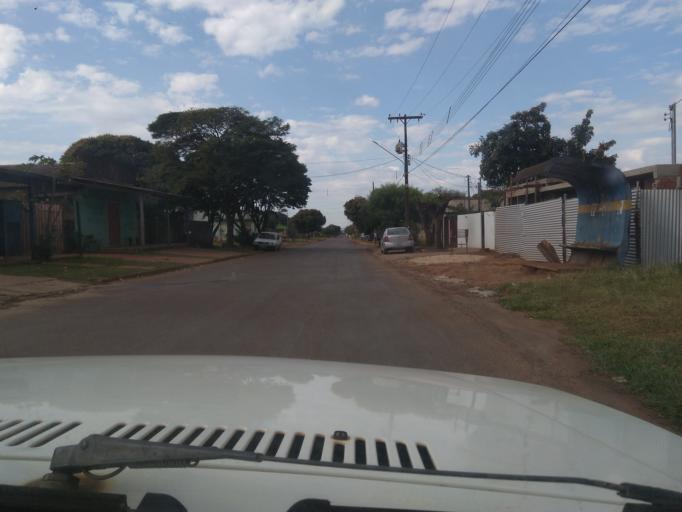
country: PY
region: Amambay
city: Pedro Juan Caballero
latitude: -22.5692
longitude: -55.6905
